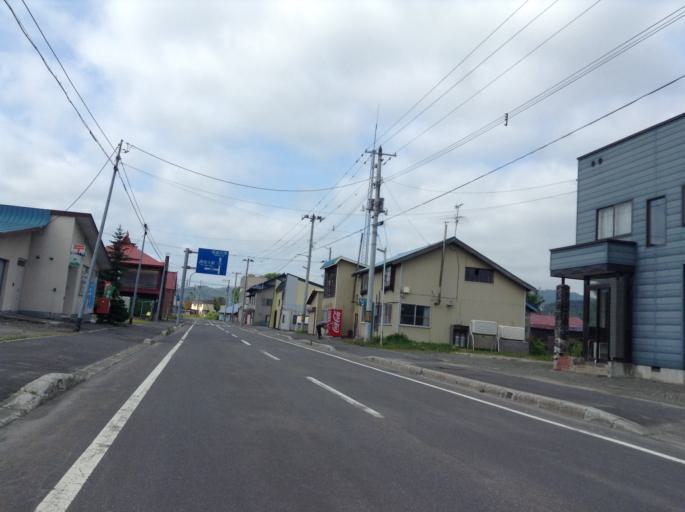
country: JP
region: Hokkaido
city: Nayoro
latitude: 44.7452
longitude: 142.0482
